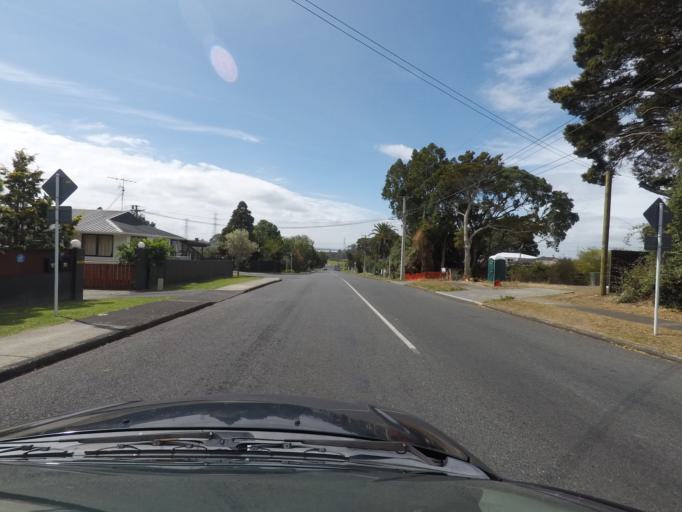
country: NZ
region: Auckland
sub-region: Auckland
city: Rosebank
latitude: -36.8971
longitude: 174.6681
